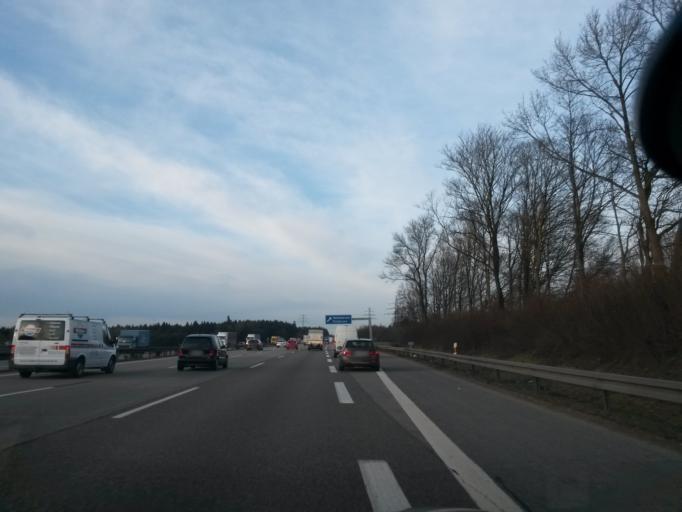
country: DE
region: Bavaria
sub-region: Upper Bavaria
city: Putzbrunn
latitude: 48.0680
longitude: 11.7187
